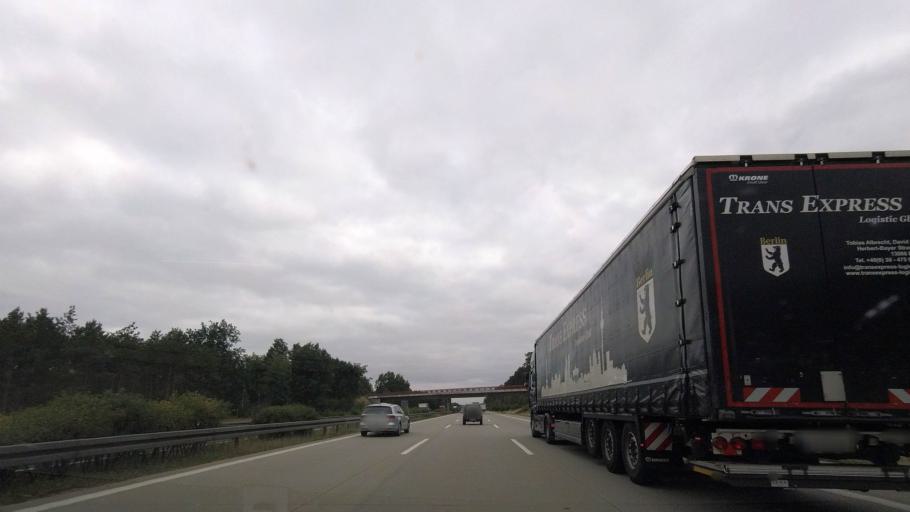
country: DE
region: Brandenburg
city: Grunheide
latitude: 52.3988
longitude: 13.7865
